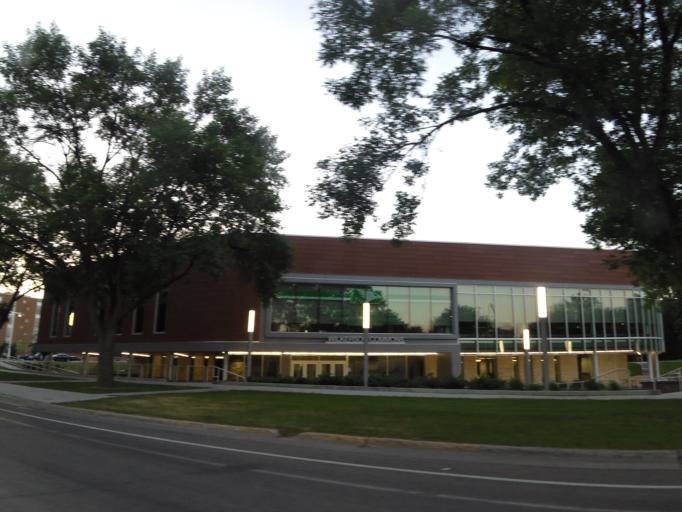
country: US
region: North Dakota
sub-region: Grand Forks County
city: Grand Forks
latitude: 47.9223
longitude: -97.0776
